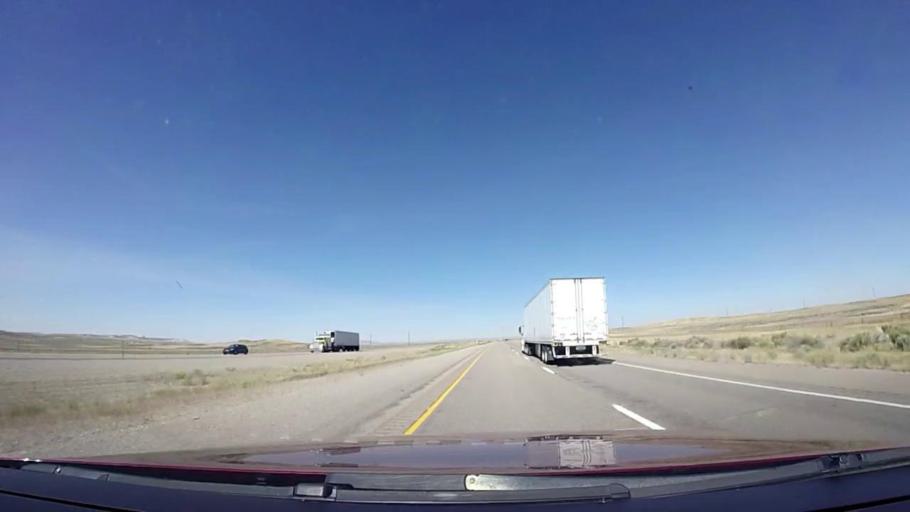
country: US
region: Wyoming
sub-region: Sweetwater County
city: Rock Springs
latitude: 41.6326
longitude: -108.3610
